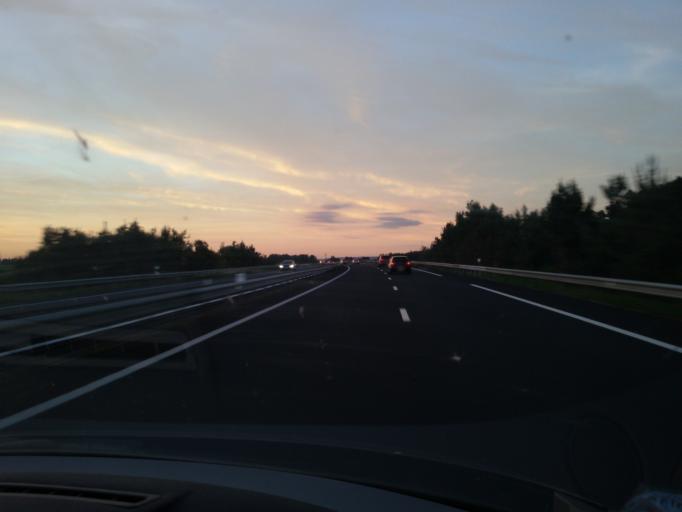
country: FR
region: Languedoc-Roussillon
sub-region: Departement de la Lozere
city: Le Malzieu-Ville
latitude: 44.9029
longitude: 3.2296
